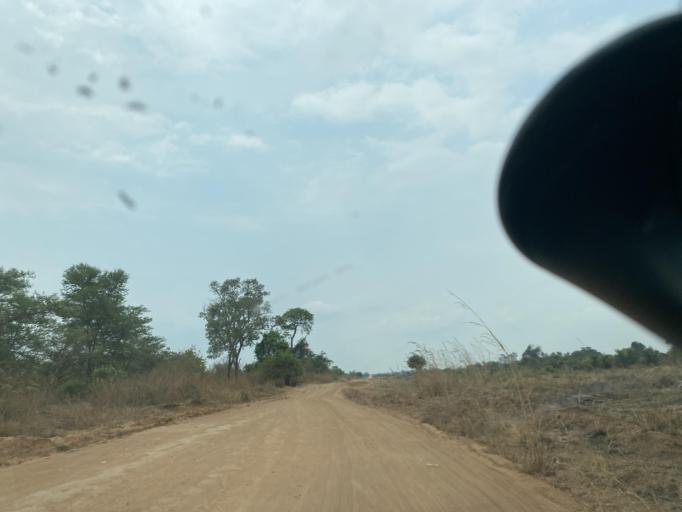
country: ZM
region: Lusaka
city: Lusaka
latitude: -15.1988
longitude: 28.3418
